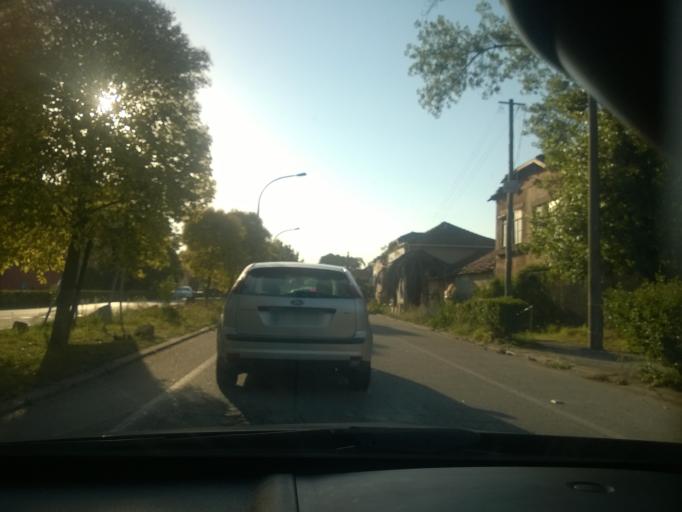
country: PT
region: Porto
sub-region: Vila Nova de Gaia
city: Vila Nova de Gaia
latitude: 41.1512
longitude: -8.6386
